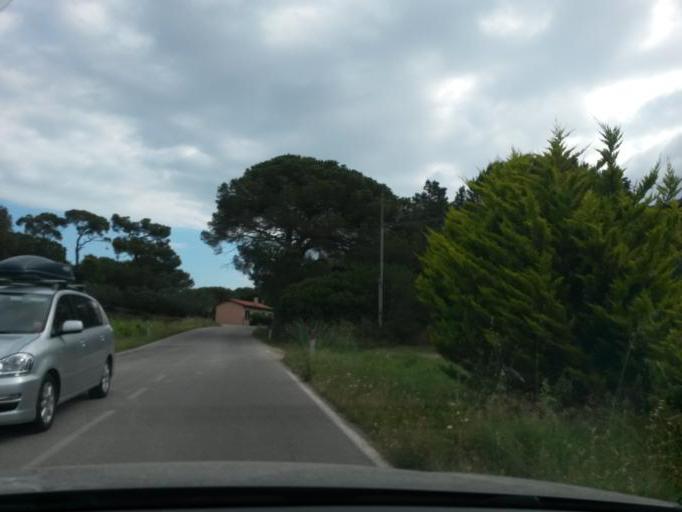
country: IT
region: Tuscany
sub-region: Provincia di Livorno
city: Portoferraio
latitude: 42.7937
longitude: 10.3534
